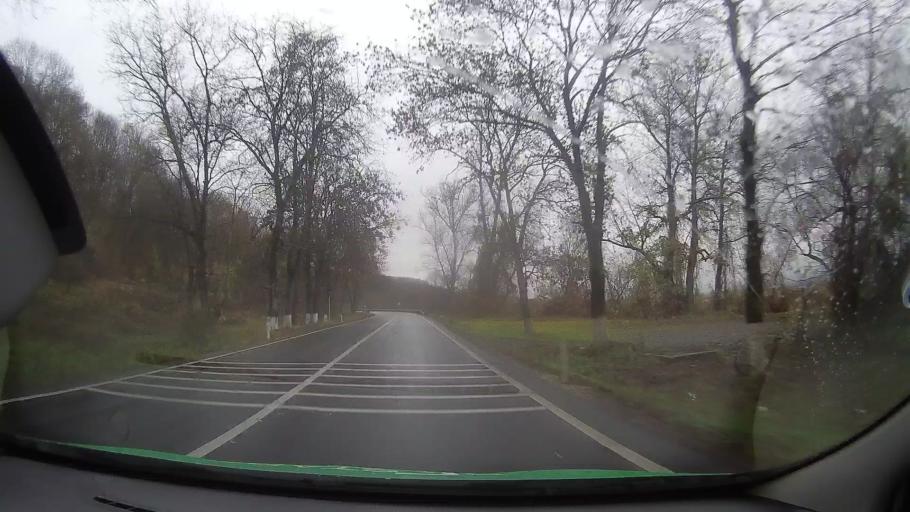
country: RO
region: Mures
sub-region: Comuna Brancovenesti
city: Brancovenesti
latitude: 46.8623
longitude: 24.7684
